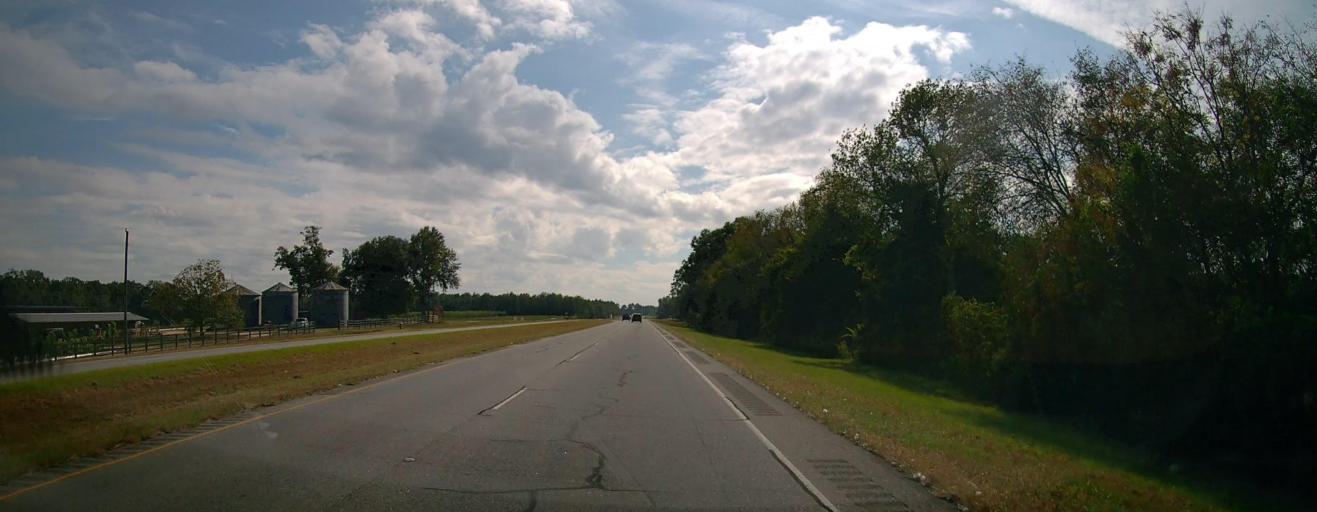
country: US
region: Georgia
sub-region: Mitchell County
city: Camilla
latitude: 31.3274
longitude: -84.1725
